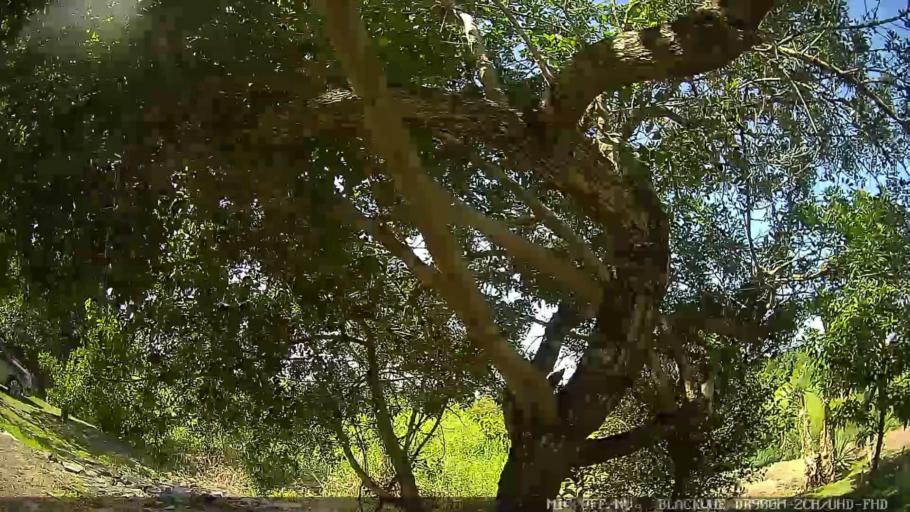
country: BR
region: Sao Paulo
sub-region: Itanhaem
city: Itanhaem
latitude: -24.2119
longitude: -46.8554
